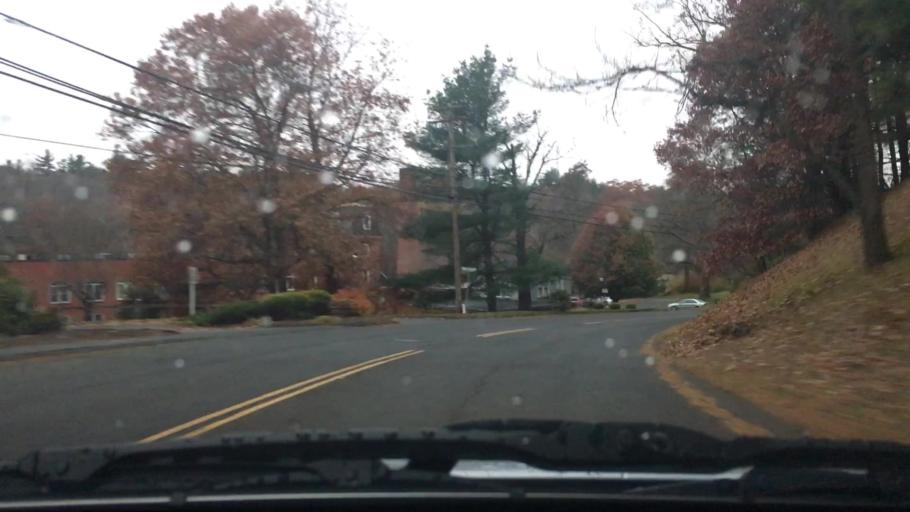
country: US
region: Massachusetts
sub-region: Hampden County
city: Westfield
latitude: 42.1202
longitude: -72.7840
